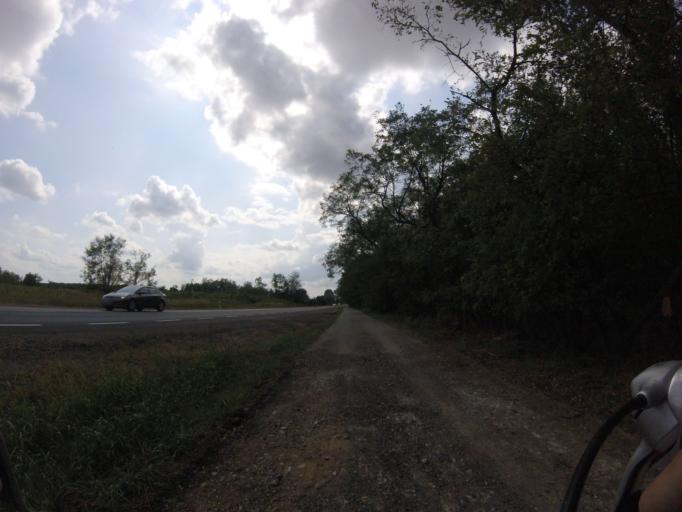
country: HU
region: Szabolcs-Szatmar-Bereg
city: Nyirpazony
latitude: 47.9769
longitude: 21.7689
